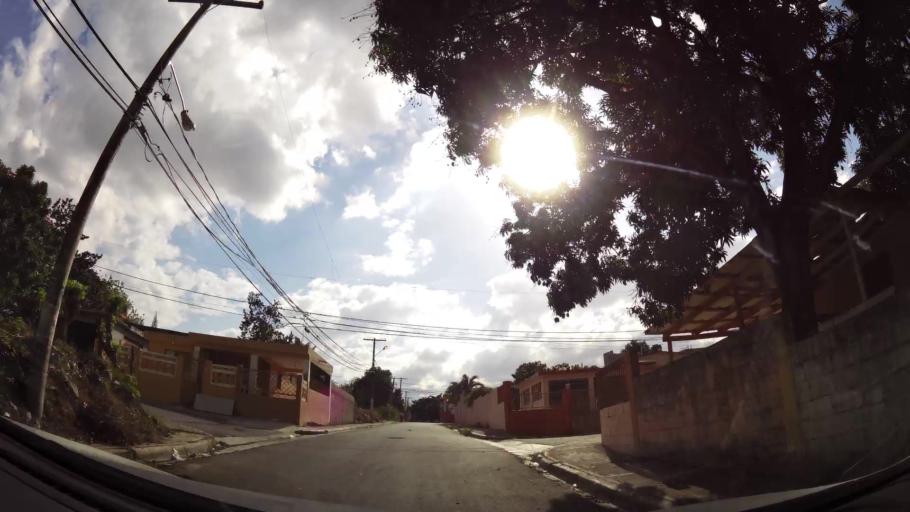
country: DO
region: Nacional
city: Ensanche Luperon
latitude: 18.5538
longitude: -69.9010
